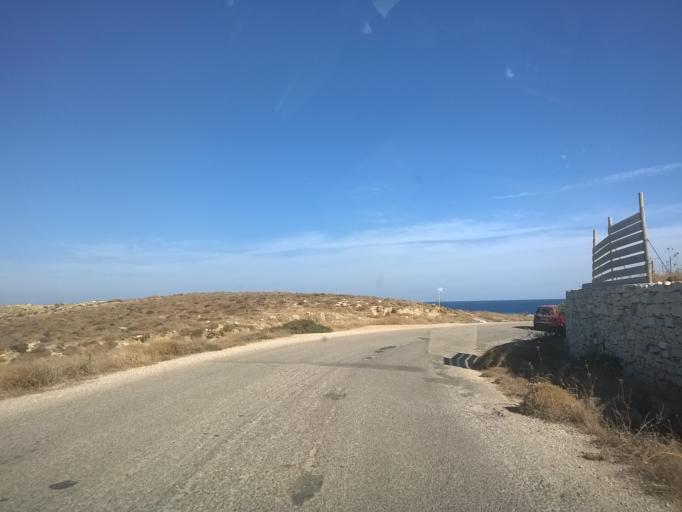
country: GR
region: South Aegean
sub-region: Nomos Kykladon
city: Naxos
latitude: 37.1397
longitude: 25.4476
